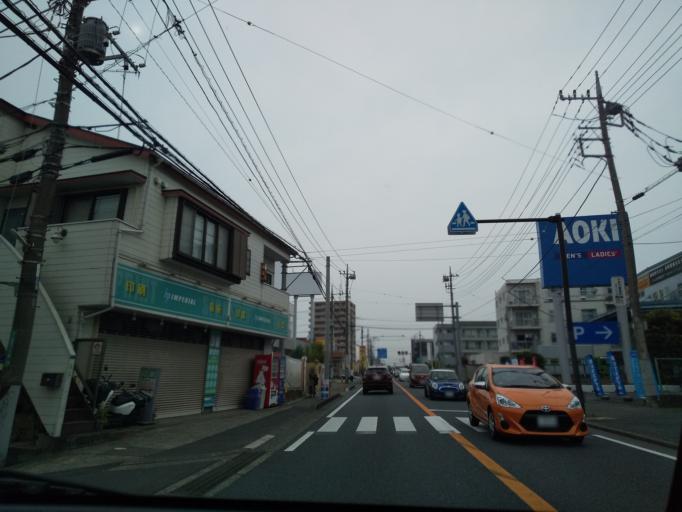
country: JP
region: Kanagawa
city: Zama
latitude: 35.5069
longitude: 139.4167
